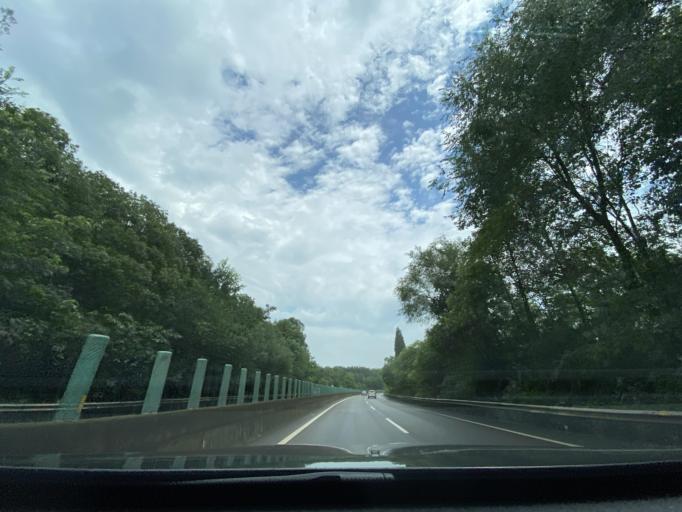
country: CN
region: Sichuan
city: Jiancheng
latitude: 30.2925
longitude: 104.5856
